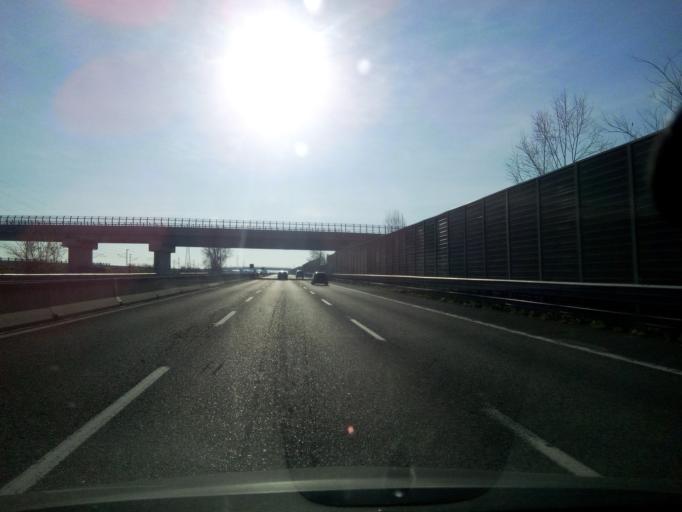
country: IT
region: Emilia-Romagna
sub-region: Provincia di Reggio Emilia
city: Massenzatico
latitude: 44.7161
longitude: 10.6916
